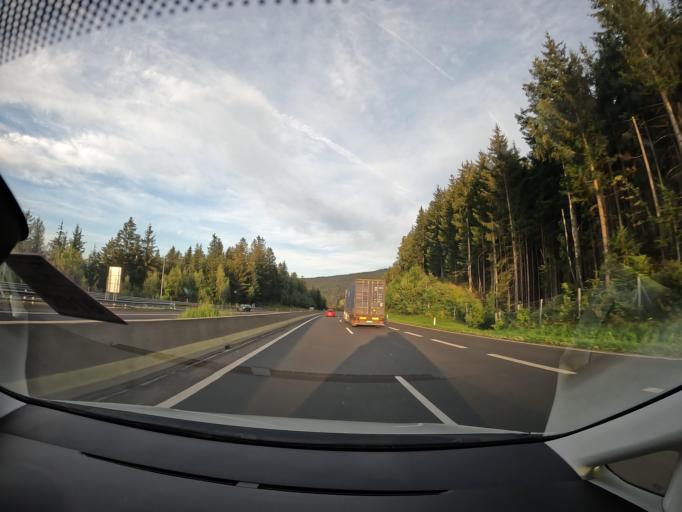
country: AT
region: Styria
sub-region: Politischer Bezirk Voitsberg
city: Voitsberg
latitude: 46.9900
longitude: 15.1150
